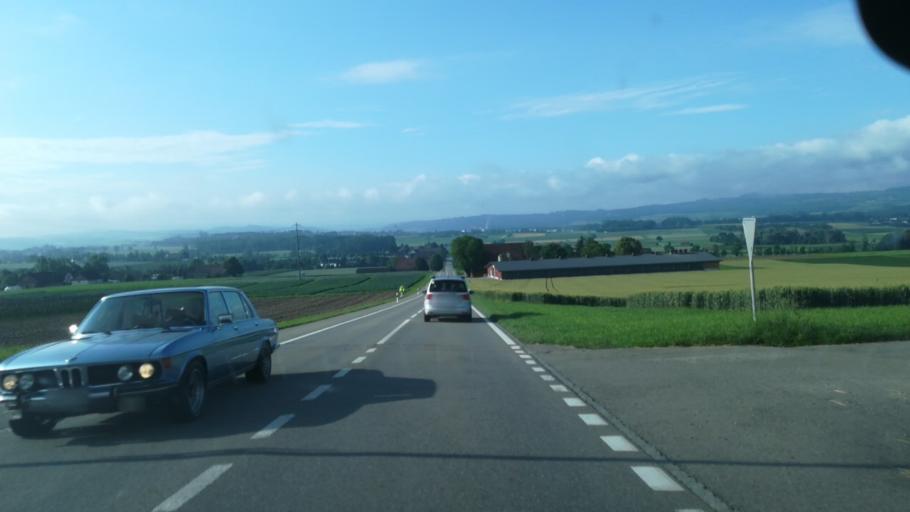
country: CH
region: Thurgau
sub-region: Weinfelden District
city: Berg
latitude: 47.5692
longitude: 9.1703
